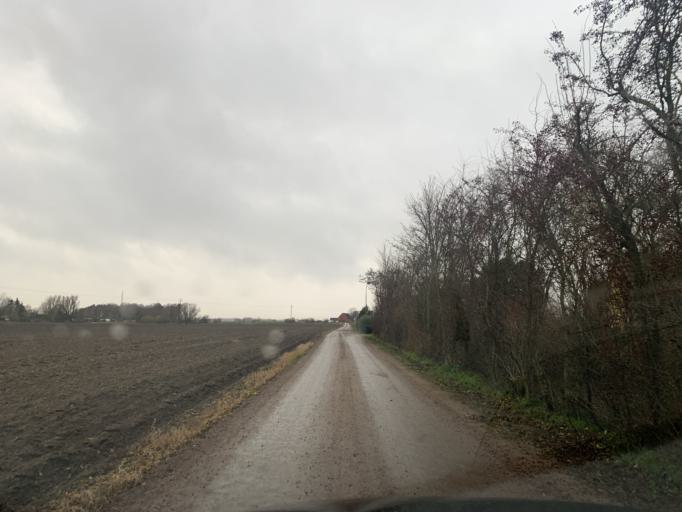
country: SE
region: Skane
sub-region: Kavlinge Kommun
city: Hofterup
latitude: 55.8382
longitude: 12.9980
